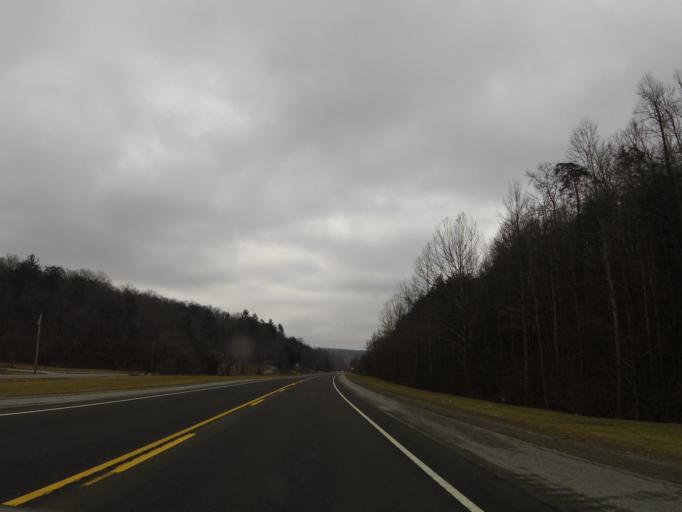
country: US
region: Tennessee
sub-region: Scott County
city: Huntsville
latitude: 36.4135
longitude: -84.4652
